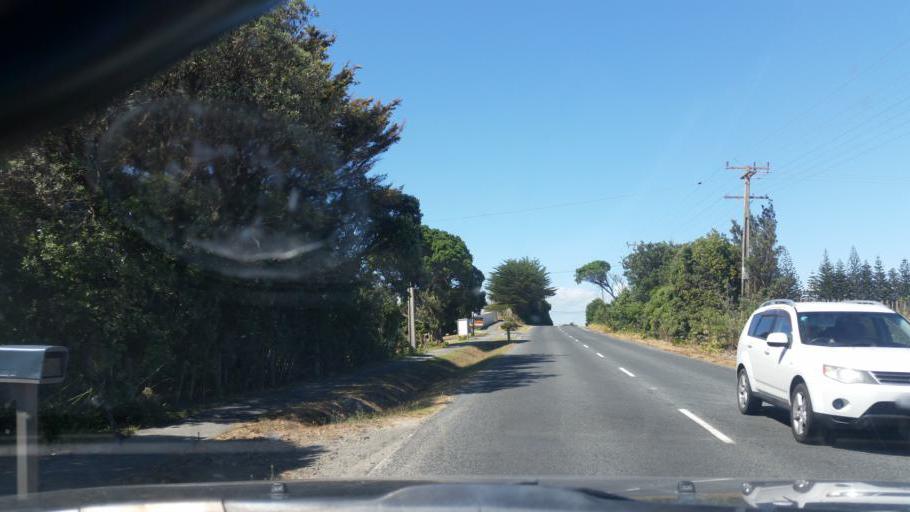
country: NZ
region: Northland
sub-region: Kaipara District
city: Dargaville
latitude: -35.9511
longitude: 173.7510
